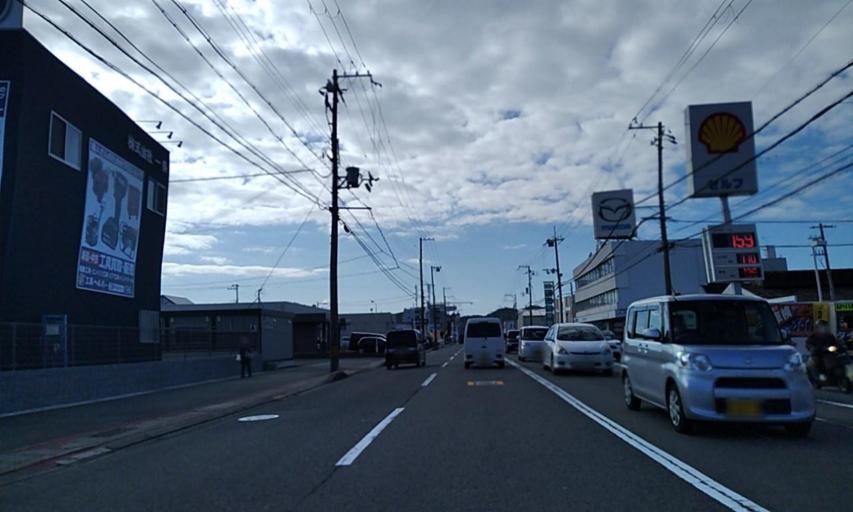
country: JP
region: Wakayama
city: Minato
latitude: 34.2122
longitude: 135.1594
